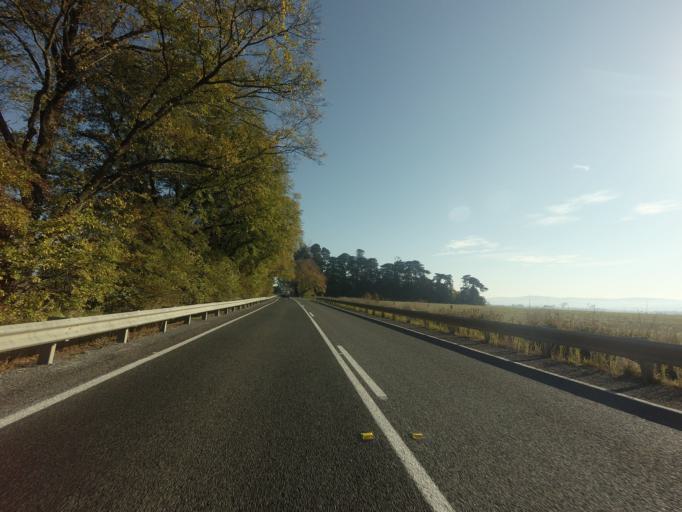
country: AU
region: Tasmania
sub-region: Northern Midlands
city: Longford
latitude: -41.5745
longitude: 147.1004
